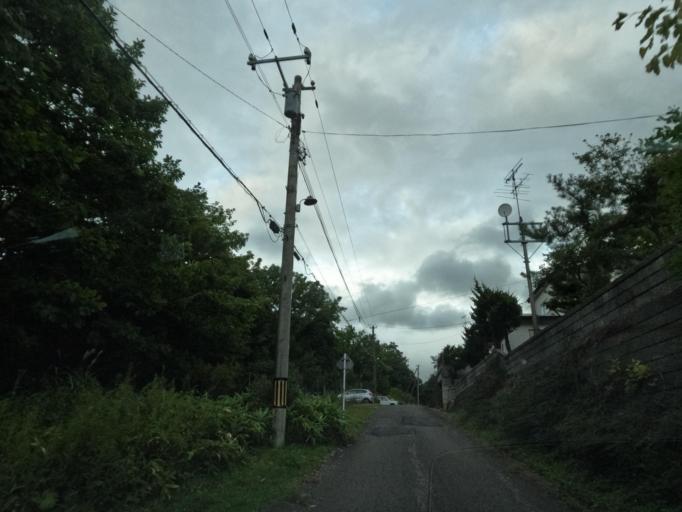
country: JP
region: Hokkaido
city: Muroran
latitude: 42.3682
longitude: 140.9659
